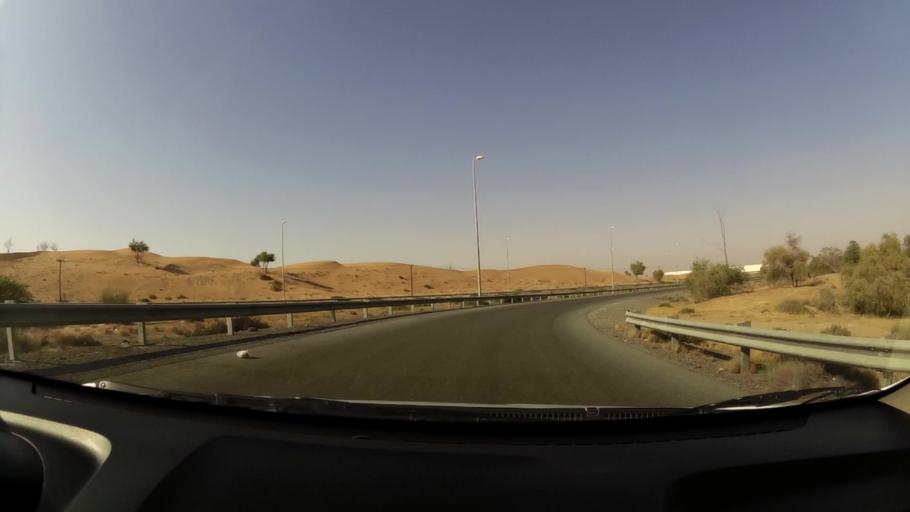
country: AE
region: Umm al Qaywayn
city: Umm al Qaywayn
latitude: 25.4547
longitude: 55.6128
